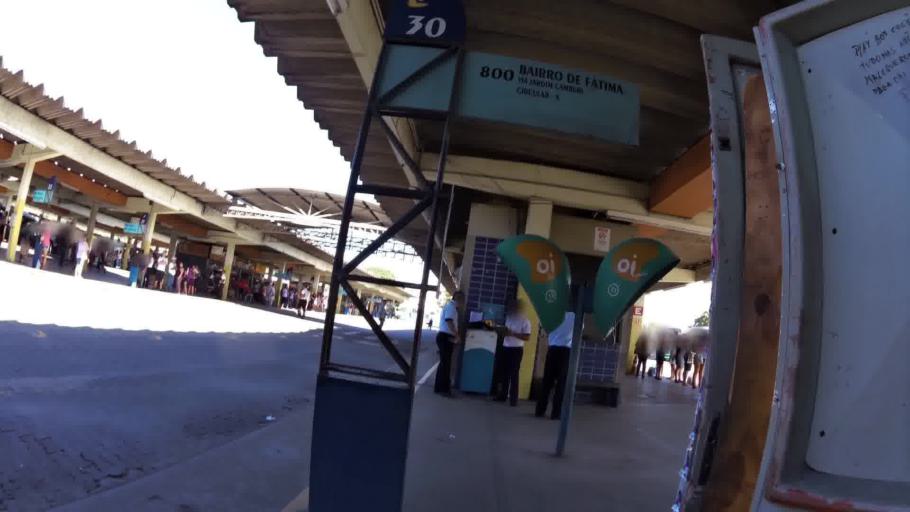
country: BR
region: Espirito Santo
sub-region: Vila Velha
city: Vila Velha
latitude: -20.2306
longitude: -40.2703
